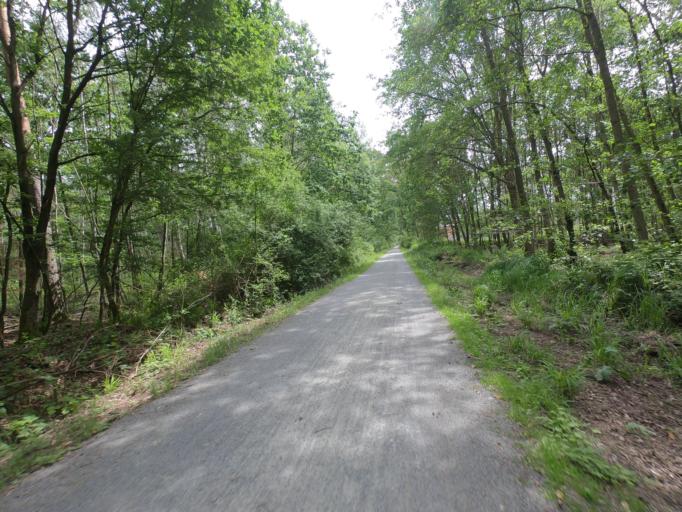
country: DE
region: Hesse
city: Langen
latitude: 50.0110
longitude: 8.6516
